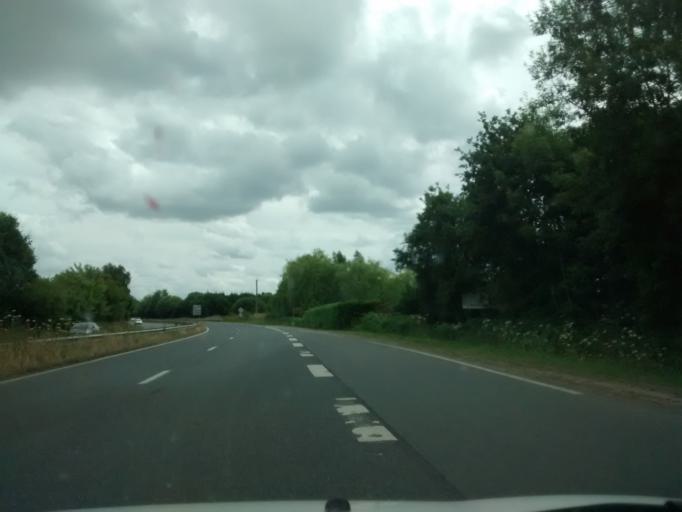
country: FR
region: Brittany
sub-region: Departement des Cotes-d'Armor
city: Cavan
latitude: 48.6558
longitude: -3.3357
